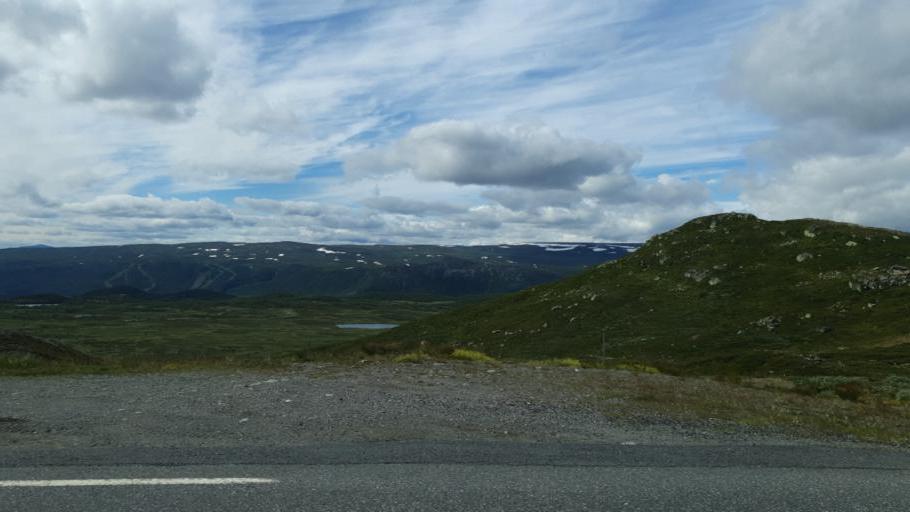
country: NO
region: Oppland
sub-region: Vestre Slidre
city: Slidre
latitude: 61.2818
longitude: 8.8380
